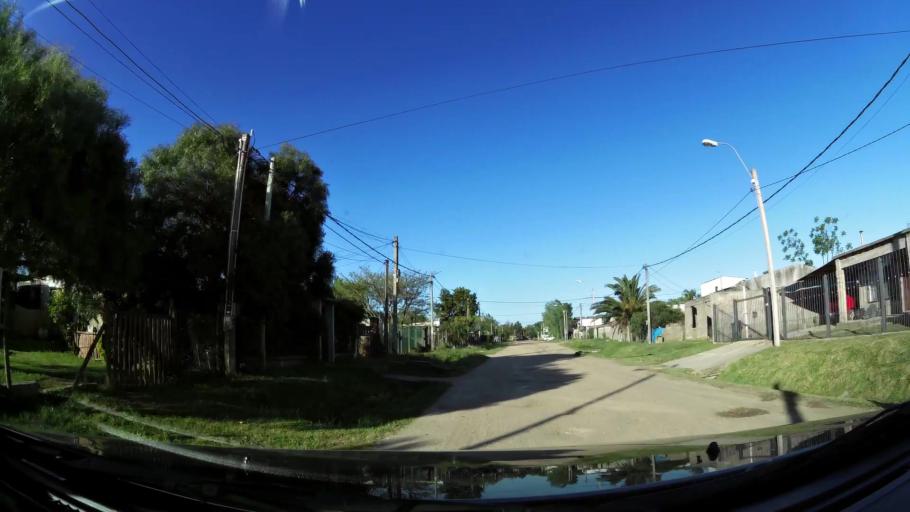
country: UY
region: Canelones
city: Paso de Carrasco
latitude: -34.8522
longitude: -56.0531
